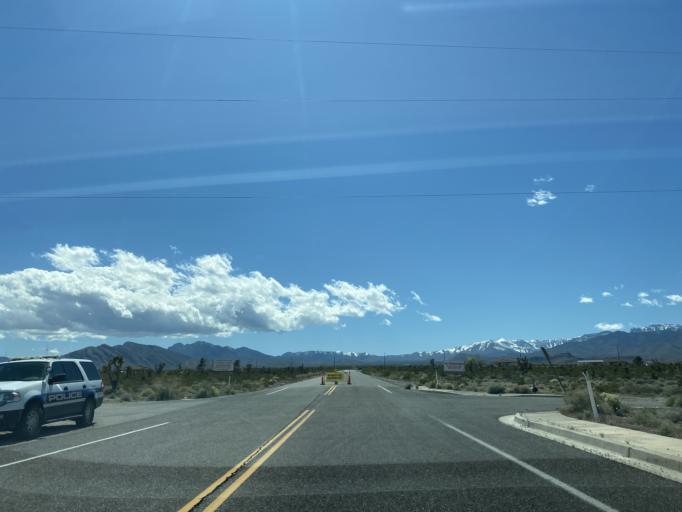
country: US
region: Nevada
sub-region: Clark County
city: Summerlin South
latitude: 36.3593
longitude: -115.3550
